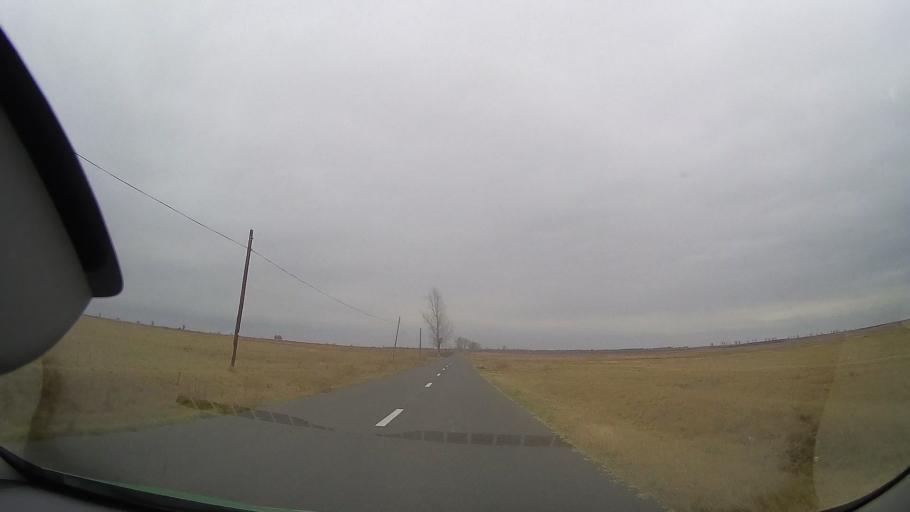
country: RO
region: Braila
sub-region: Comuna Budesti
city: Tataru
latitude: 44.8303
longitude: 27.4087
